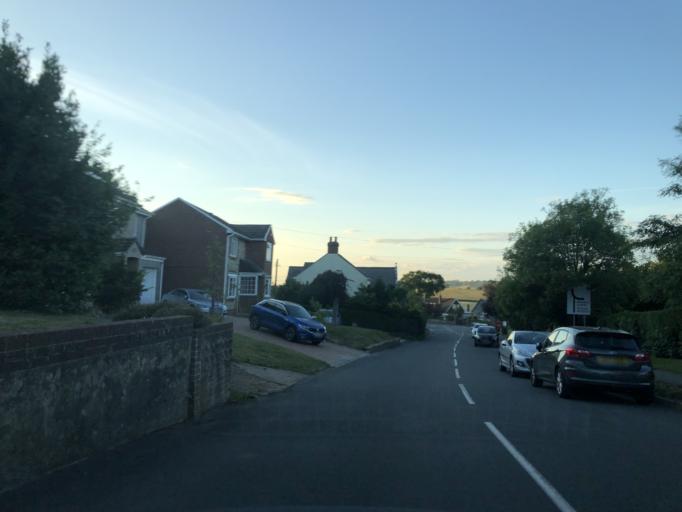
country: GB
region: England
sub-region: Isle of Wight
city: Newport
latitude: 50.6538
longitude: -1.2836
